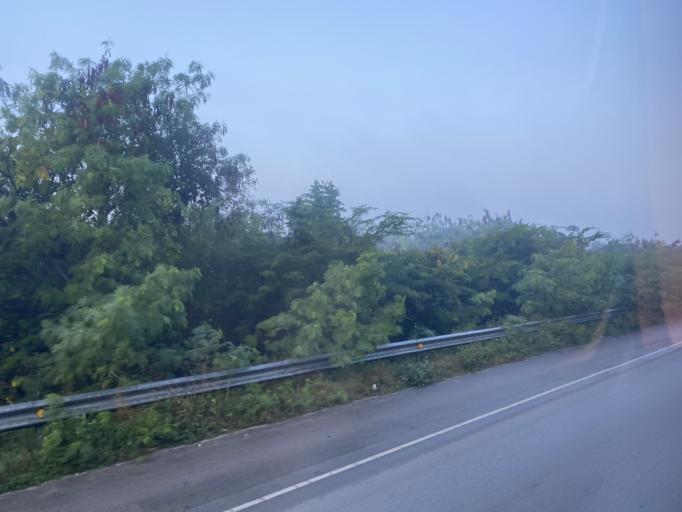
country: DO
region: La Altagracia
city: Otra Banda
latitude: 18.7366
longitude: -68.5107
